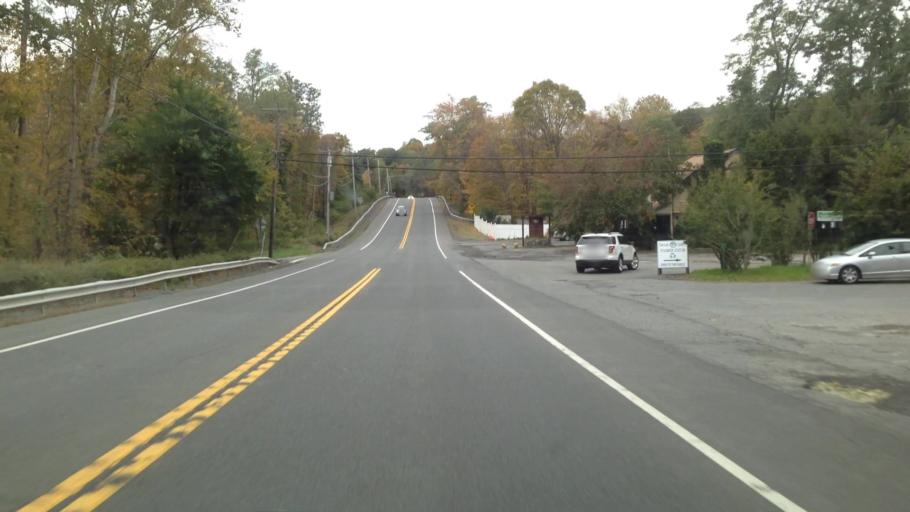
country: US
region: New York
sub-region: Dutchess County
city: Hyde Park
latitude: 41.7951
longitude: -73.9597
